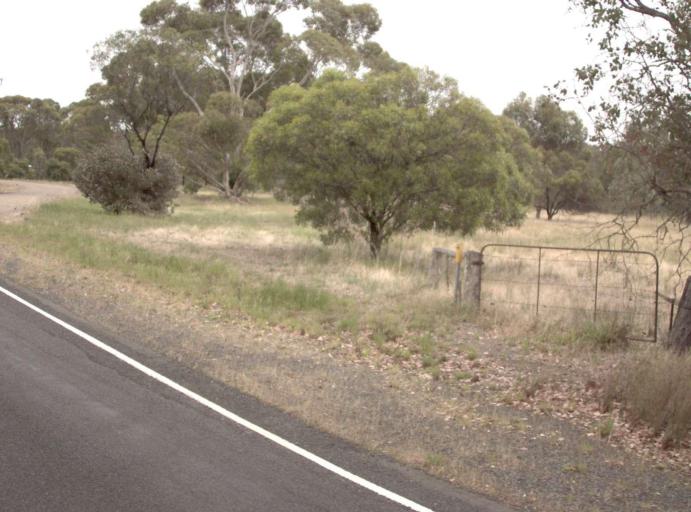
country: AU
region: Victoria
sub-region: Wellington
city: Heyfield
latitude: -37.9643
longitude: 146.7759
